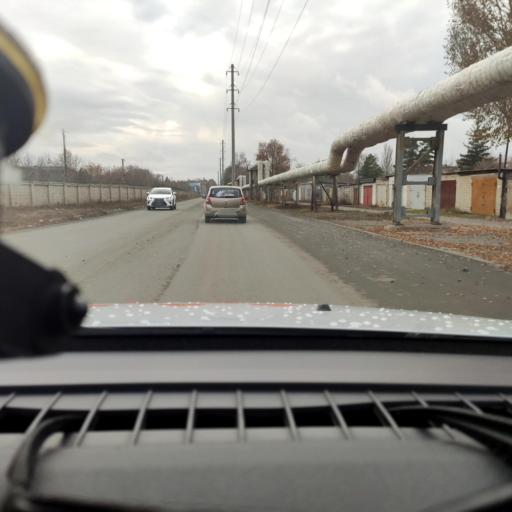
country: RU
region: Samara
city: Chapayevsk
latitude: 52.9824
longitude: 49.7223
